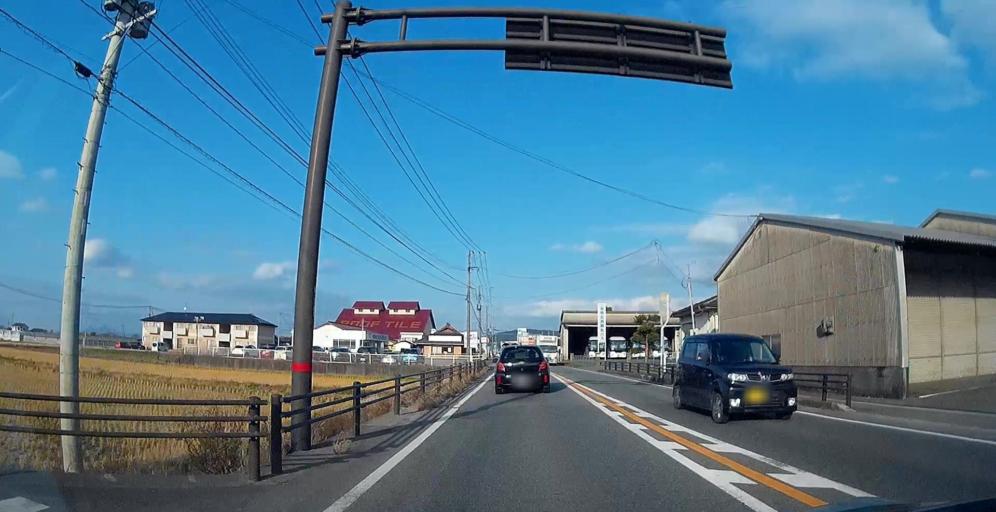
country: JP
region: Kumamoto
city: Matsubase
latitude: 32.5835
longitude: 130.6993
